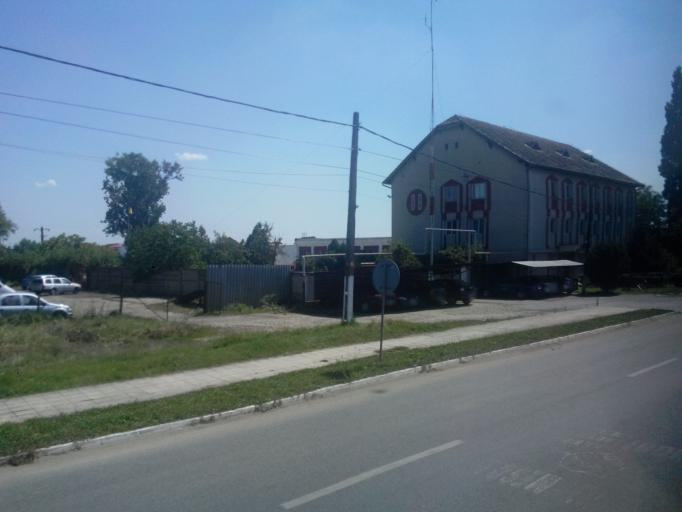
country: RO
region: Timis
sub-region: Municipiul Lugoj
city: Lugoj
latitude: 45.6965
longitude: 21.9254
